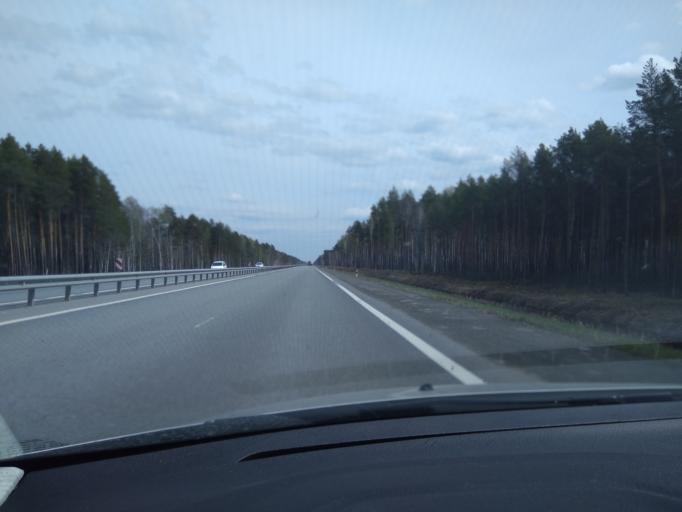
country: RU
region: Sverdlovsk
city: Yushala
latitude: 57.0951
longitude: 64.3837
